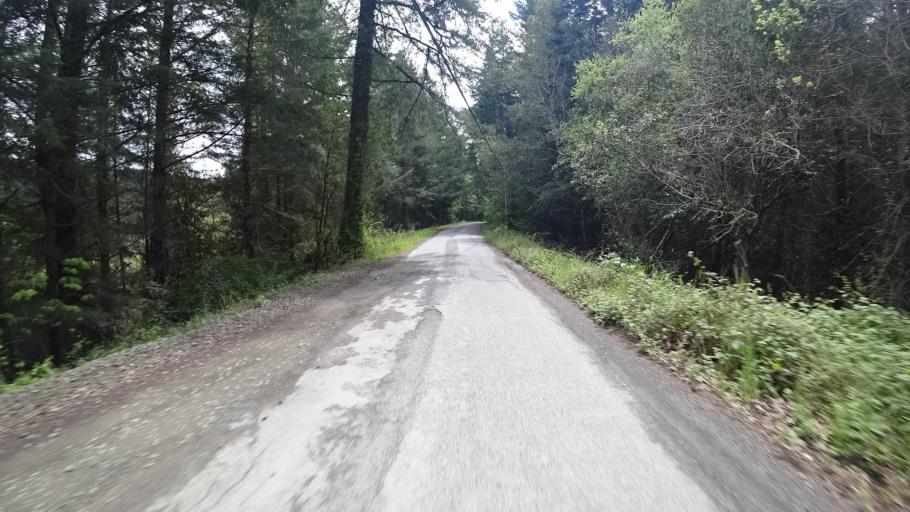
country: US
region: California
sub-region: Humboldt County
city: Blue Lake
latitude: 40.7888
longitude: -123.8813
